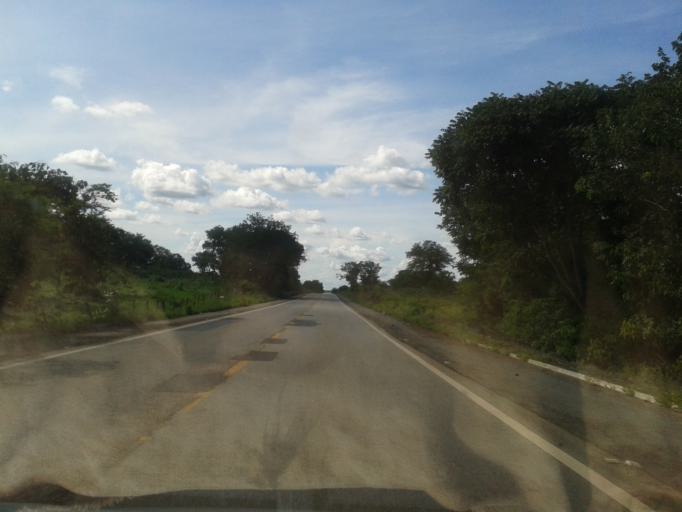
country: BR
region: Goias
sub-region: Mozarlandia
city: Mozarlandia
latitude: -15.2291
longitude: -50.5211
